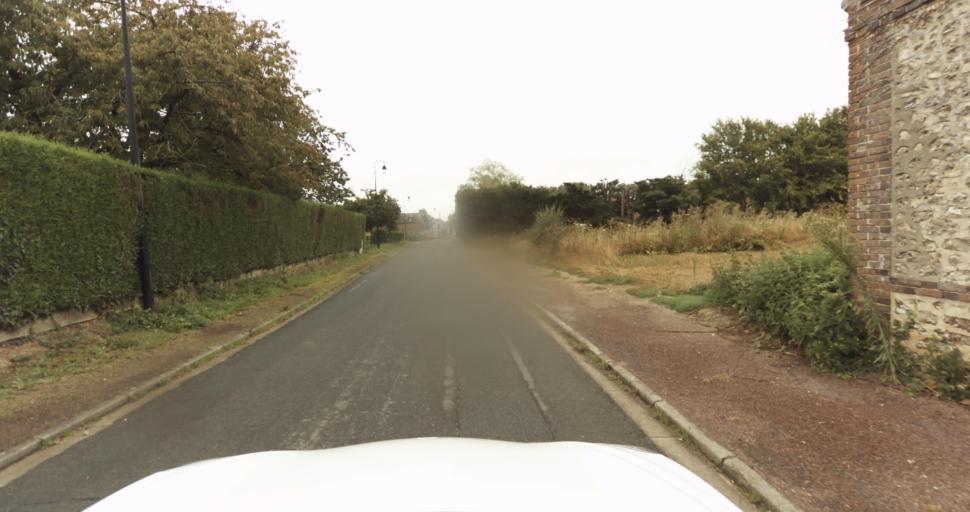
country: FR
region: Haute-Normandie
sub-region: Departement de l'Eure
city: Aviron
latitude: 49.0771
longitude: 1.0877
